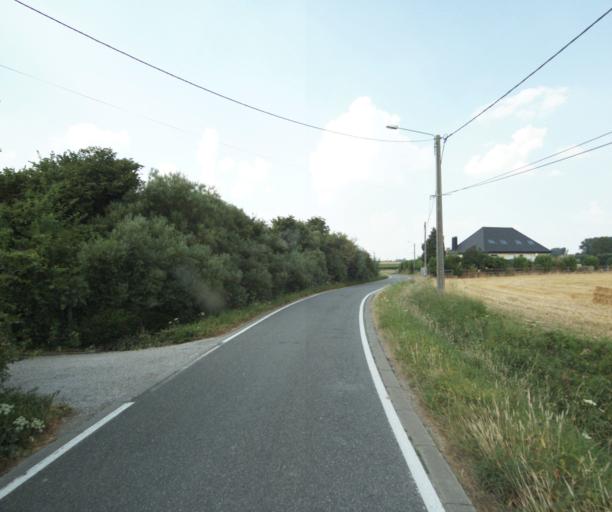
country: FR
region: Nord-Pas-de-Calais
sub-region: Departement du Nord
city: Linselles
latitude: 50.7267
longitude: 3.0595
